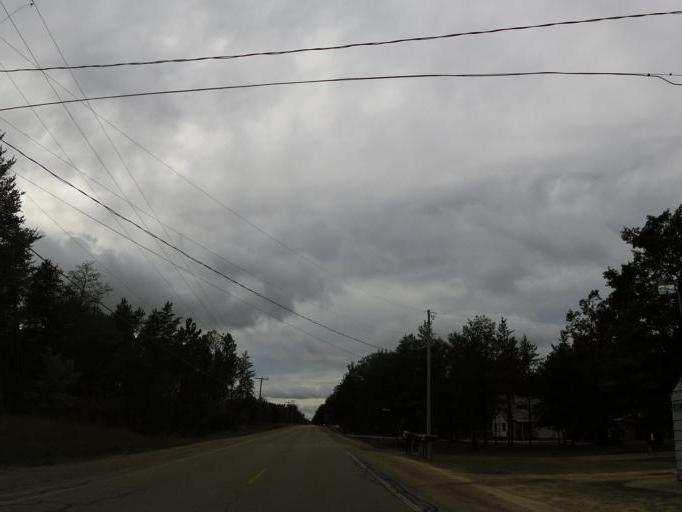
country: US
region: Michigan
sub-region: Roscommon County
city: Saint Helen
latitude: 44.3490
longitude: -84.4174
